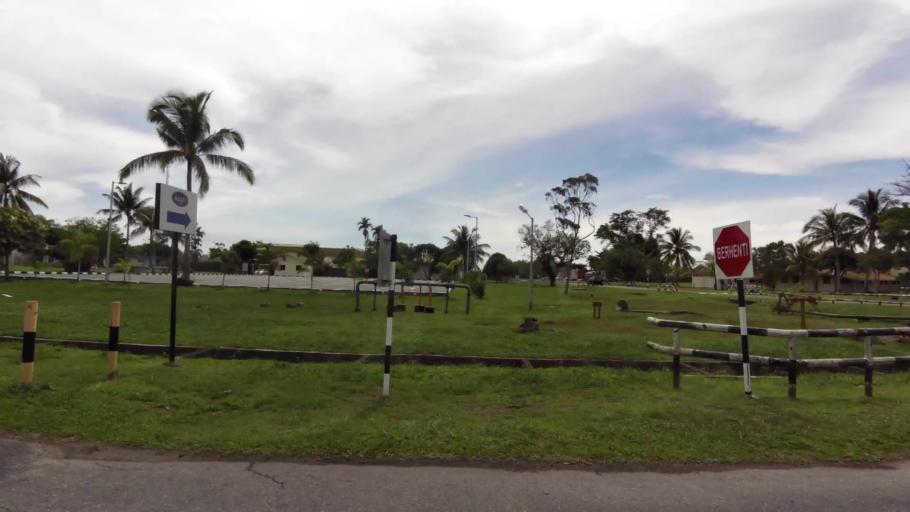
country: BN
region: Belait
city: Seria
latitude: 4.6059
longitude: 114.3128
